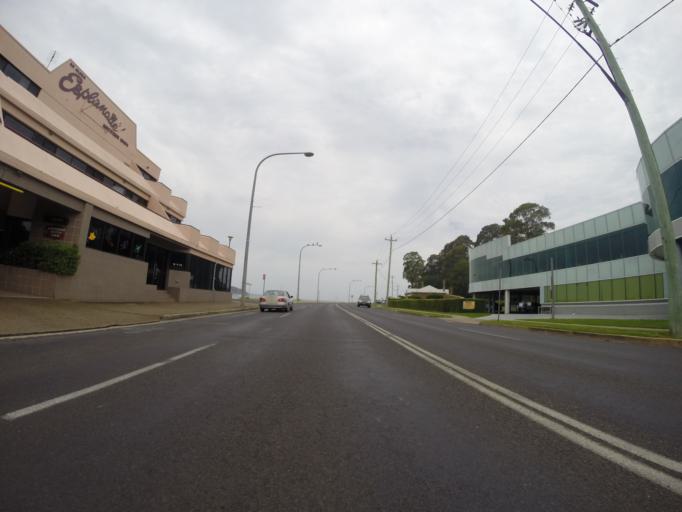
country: AU
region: New South Wales
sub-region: Eurobodalla
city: Batemans Bay
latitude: -35.7085
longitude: 150.1785
